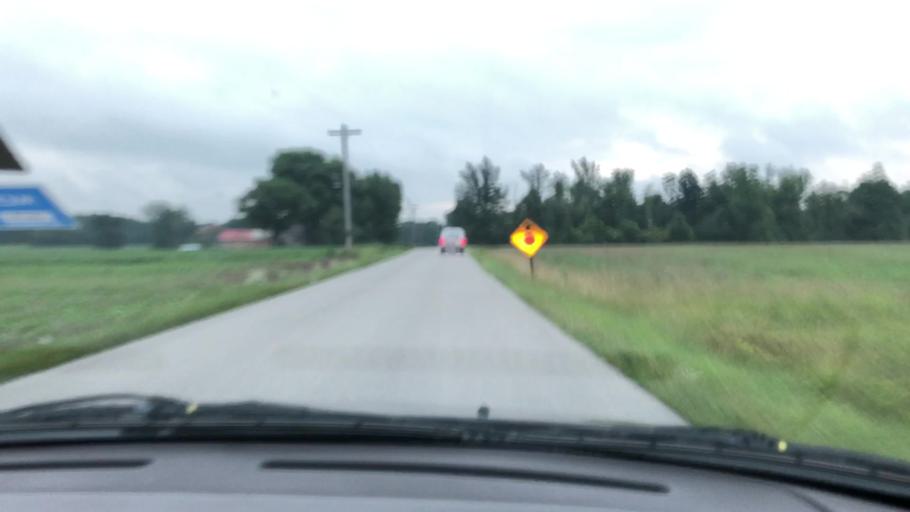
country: US
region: Indiana
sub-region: Greene County
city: Linton
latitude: 38.9767
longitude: -87.3012
